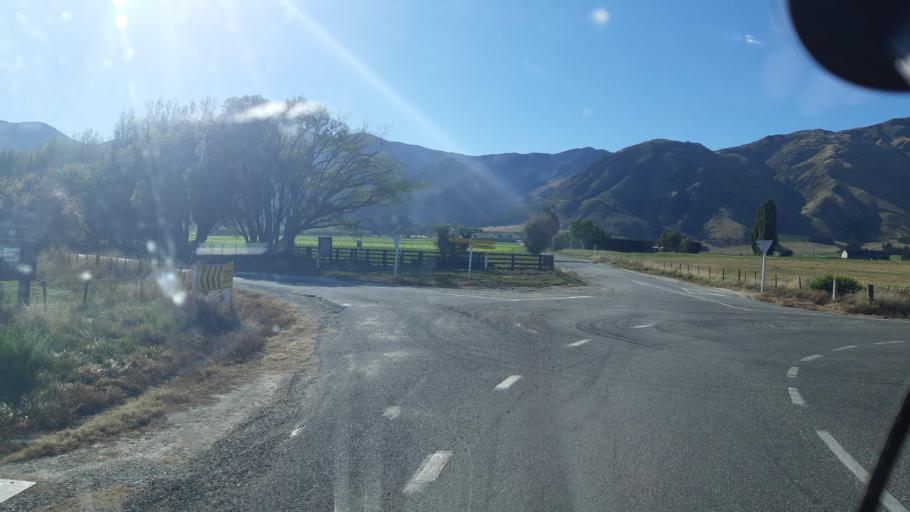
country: NZ
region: Otago
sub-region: Queenstown-Lakes District
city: Wanaka
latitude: -44.6185
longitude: 169.2917
